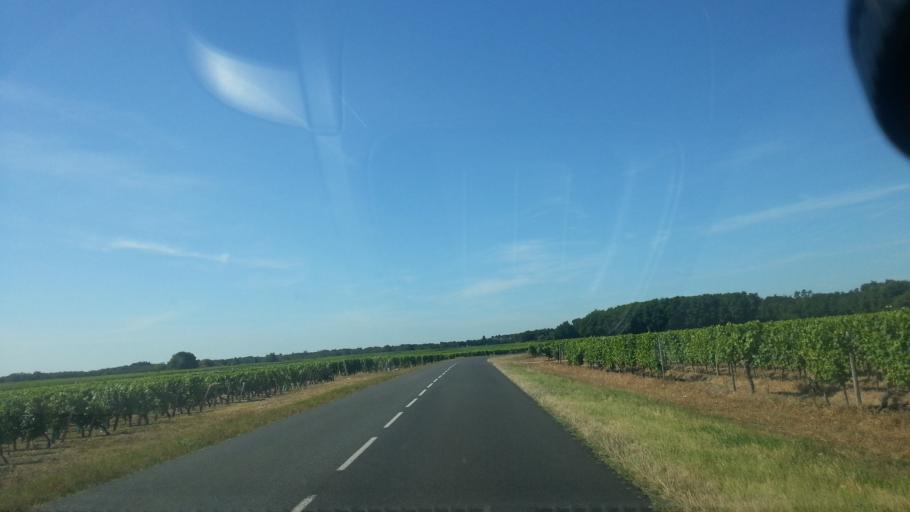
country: FR
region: Aquitaine
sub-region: Departement de la Gironde
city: Podensac
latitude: 44.6363
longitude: -0.3632
